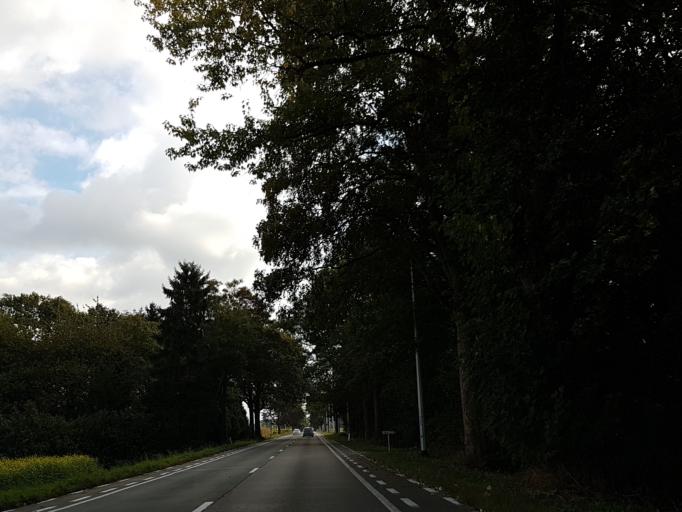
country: BE
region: Flanders
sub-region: Provincie Vlaams-Brabant
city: Boutersem
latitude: 50.8525
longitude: 4.8040
